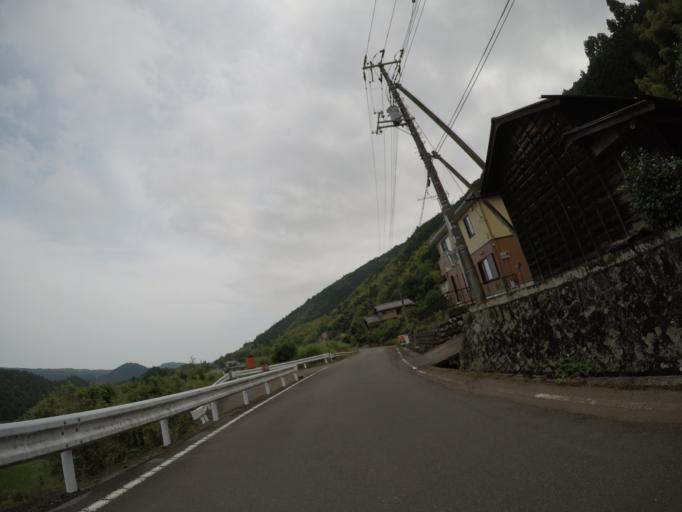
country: JP
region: Shizuoka
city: Fujinomiya
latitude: 35.2419
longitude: 138.5556
